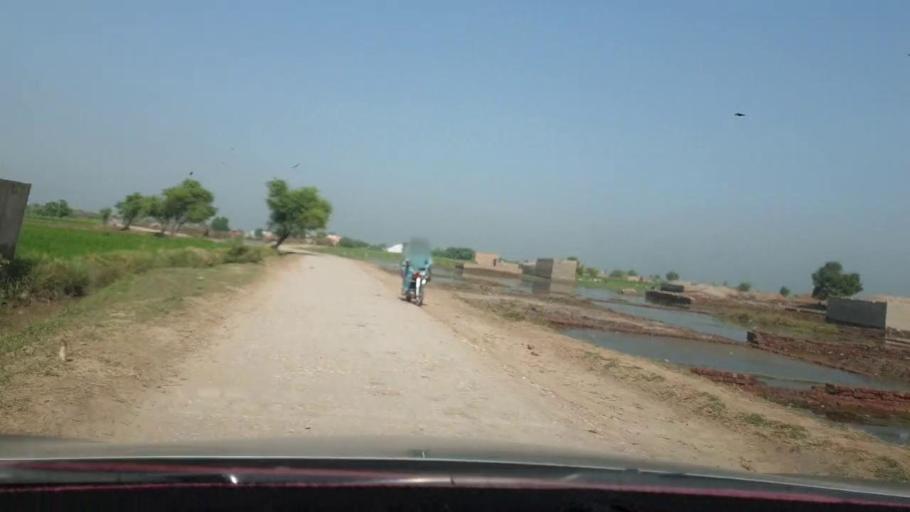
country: PK
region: Sindh
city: Kambar
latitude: 27.5984
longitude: 67.9843
